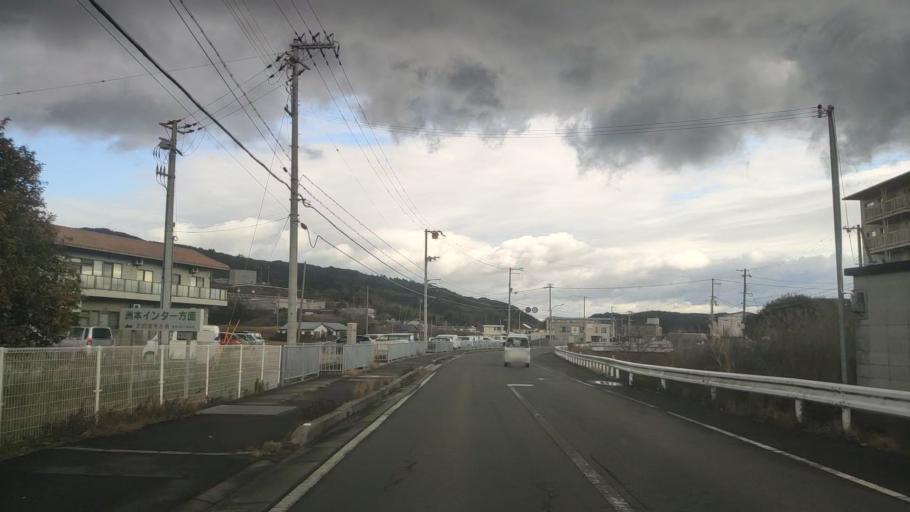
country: JP
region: Hyogo
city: Sumoto
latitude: 34.3313
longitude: 134.8652
